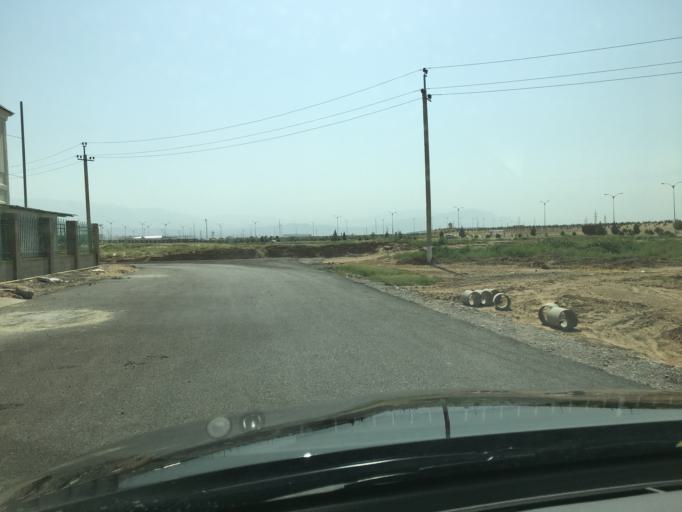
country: TM
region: Ahal
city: Ashgabat
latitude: 38.0020
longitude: 58.3977
